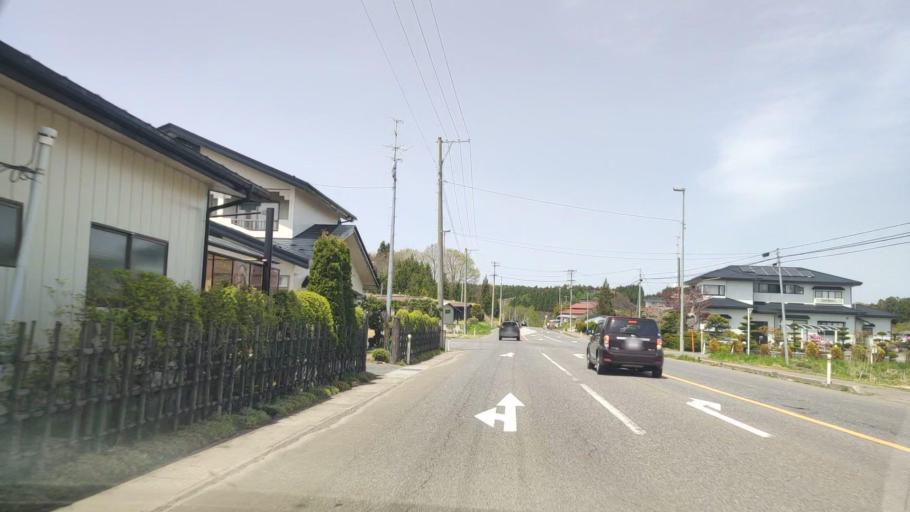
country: JP
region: Aomori
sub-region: Misawa Shi
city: Inuotose
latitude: 40.5603
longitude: 141.3848
